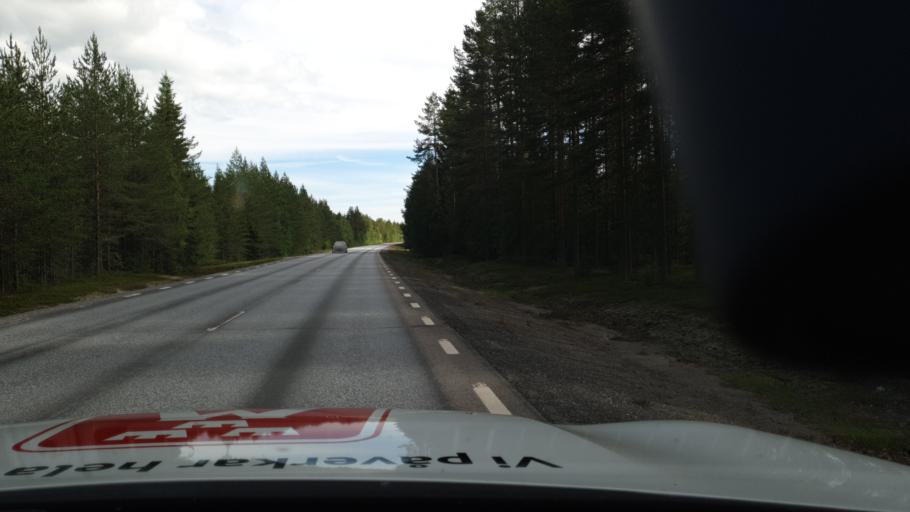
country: SE
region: Vaesterbotten
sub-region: Umea Kommun
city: Roback
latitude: 63.9612
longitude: 20.1307
